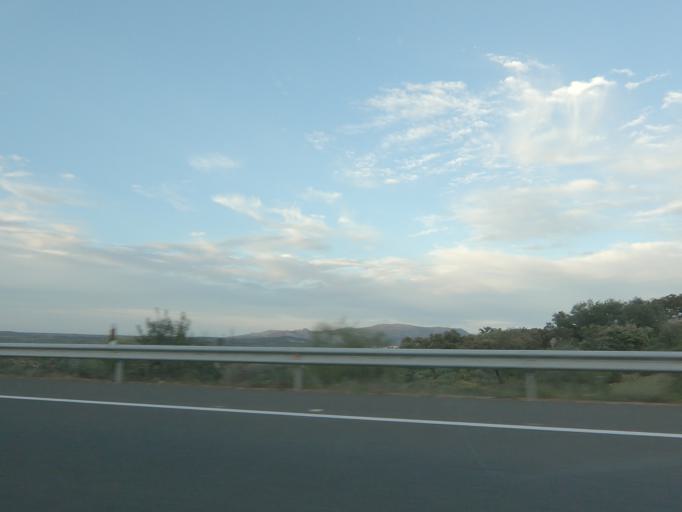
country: ES
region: Extremadura
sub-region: Provincia de Caceres
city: Alcuescar
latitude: 39.1707
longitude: -6.2704
